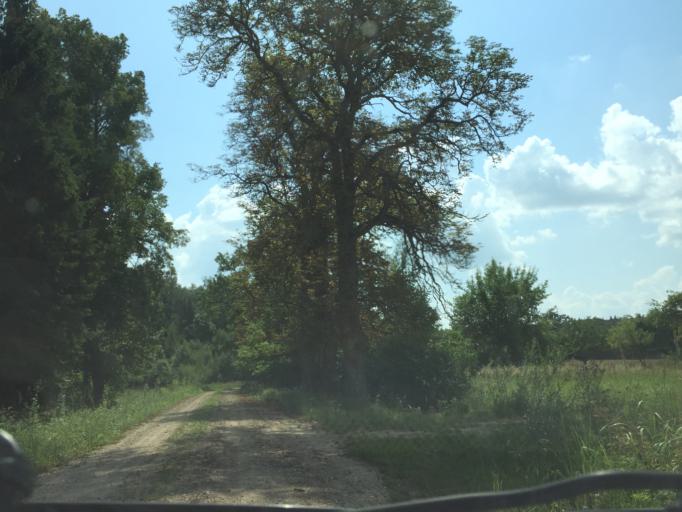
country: LT
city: Zagare
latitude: 56.3899
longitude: 23.2049
